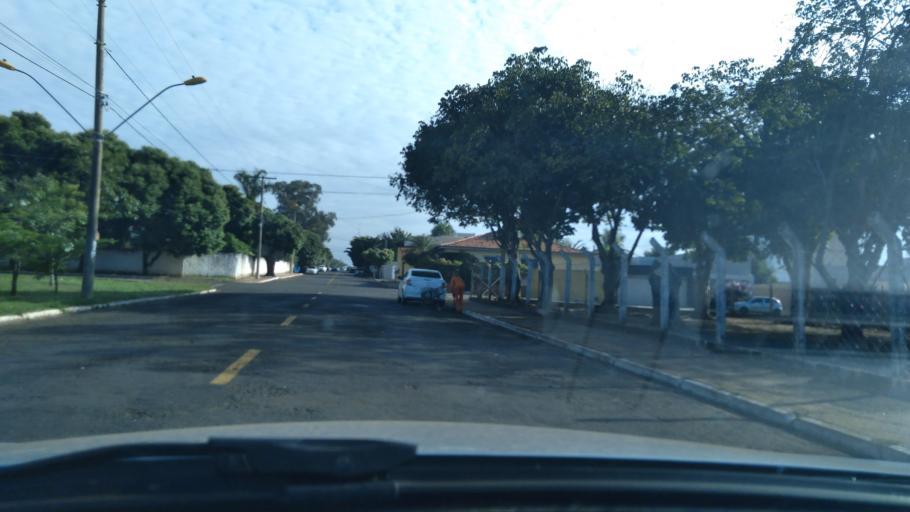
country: BR
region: Goias
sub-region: Mineiros
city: Mineiros
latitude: -17.5622
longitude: -52.5590
